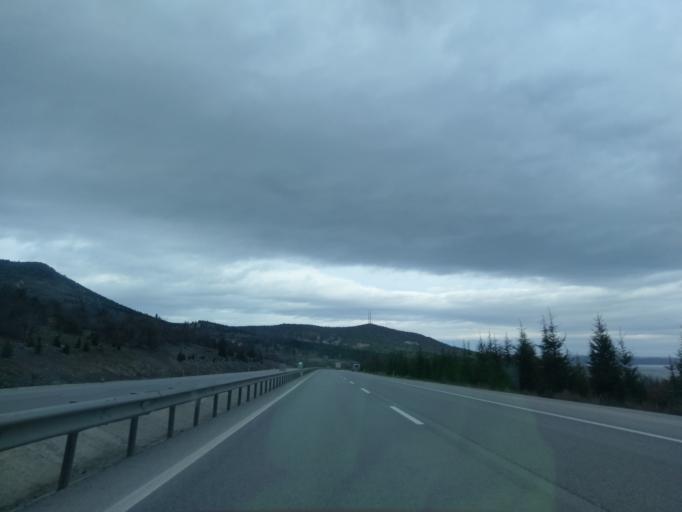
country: TR
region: Kuetahya
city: Sabuncu
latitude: 39.5983
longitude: 30.1448
